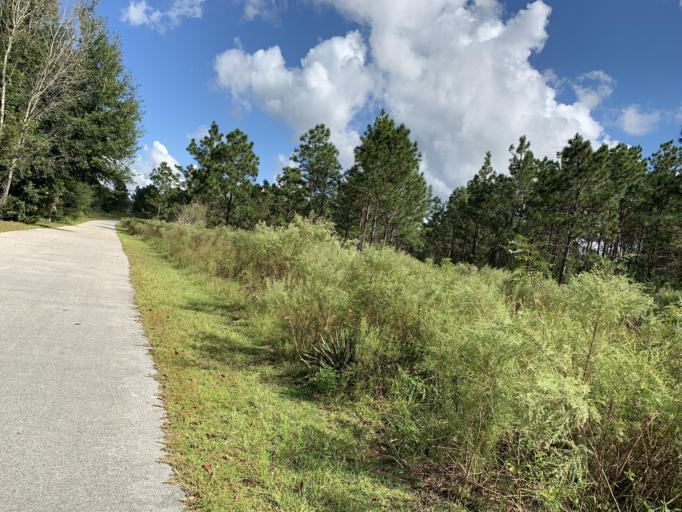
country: US
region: Florida
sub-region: Marion County
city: Silver Springs Shores
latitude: 29.1528
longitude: -82.0447
